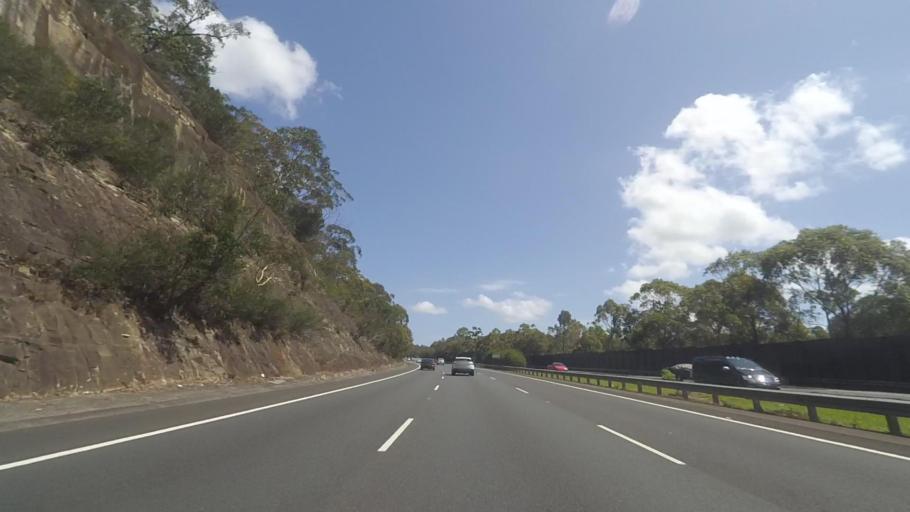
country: AU
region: New South Wales
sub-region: Ku-ring-gai
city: North Wahroonga
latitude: -33.7004
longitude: 151.1183
